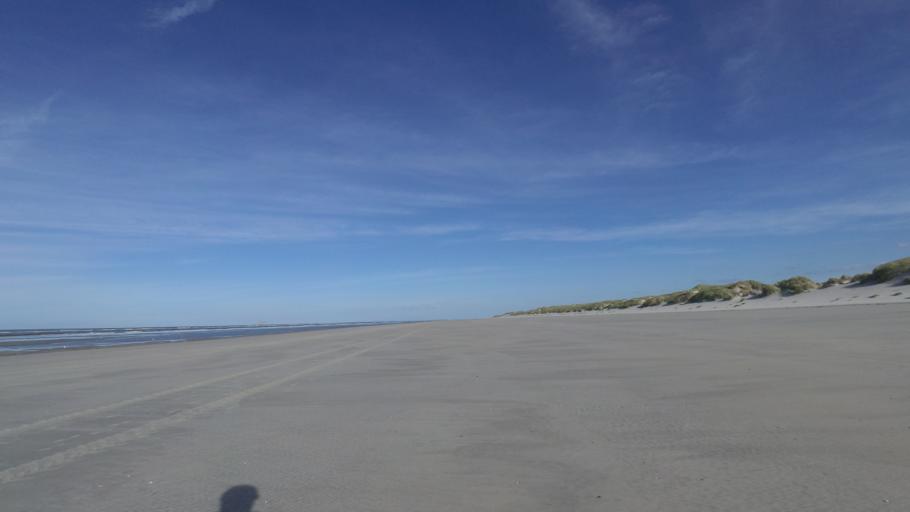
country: NL
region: Friesland
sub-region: Gemeente Ameland
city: Nes
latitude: 53.4661
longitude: 5.8726
